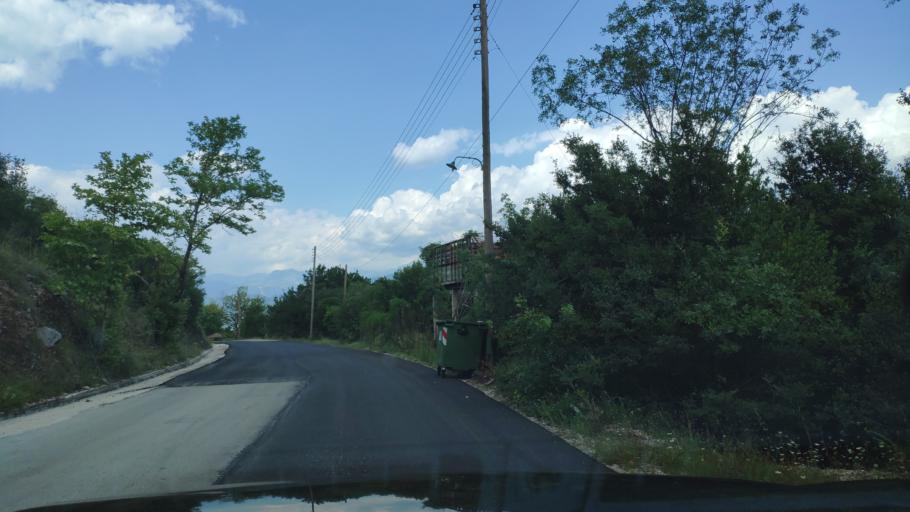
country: GR
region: Epirus
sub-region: Nomos Artas
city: Agios Dimitrios
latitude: 39.4210
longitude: 21.0131
